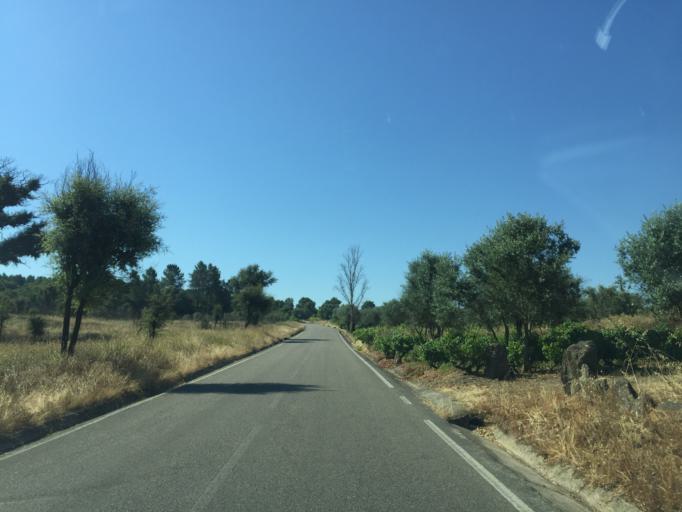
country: PT
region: Santarem
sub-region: Tomar
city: Tomar
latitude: 39.5916
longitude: -8.3282
